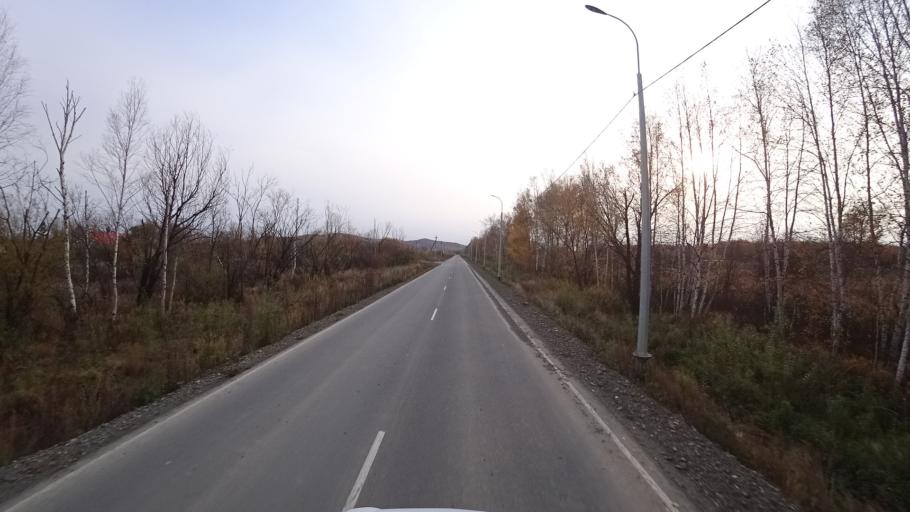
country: RU
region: Khabarovsk Krai
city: Amursk
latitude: 50.0769
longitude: 136.4919
